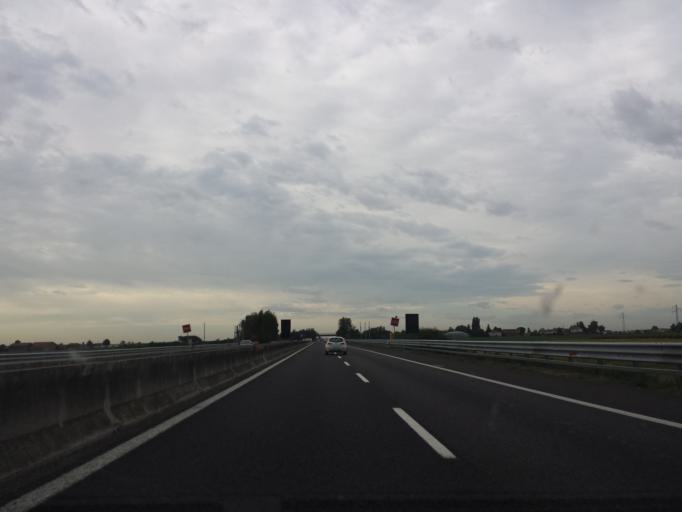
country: IT
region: Veneto
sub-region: Provincia di Padova
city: Pozzonovo
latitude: 45.1906
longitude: 11.7758
